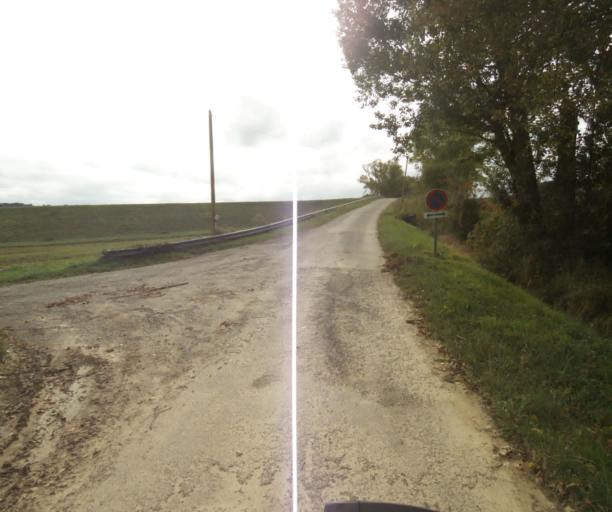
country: FR
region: Midi-Pyrenees
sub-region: Departement du Tarn-et-Garonne
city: Beaumont-de-Lomagne
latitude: 43.8167
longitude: 1.0794
